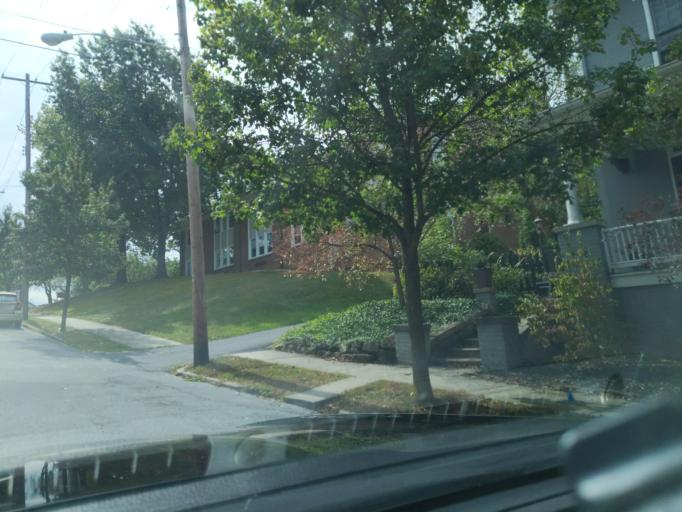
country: US
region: Pennsylvania
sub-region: Blair County
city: Hollidaysburg
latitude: 40.4325
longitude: -78.3897
